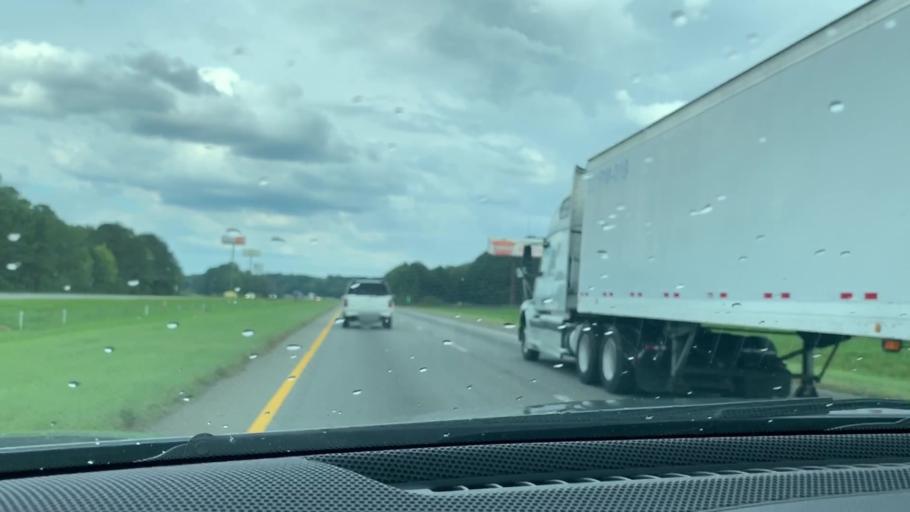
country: US
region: South Carolina
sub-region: Hampton County
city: Yemassee
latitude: 32.5953
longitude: -80.9120
